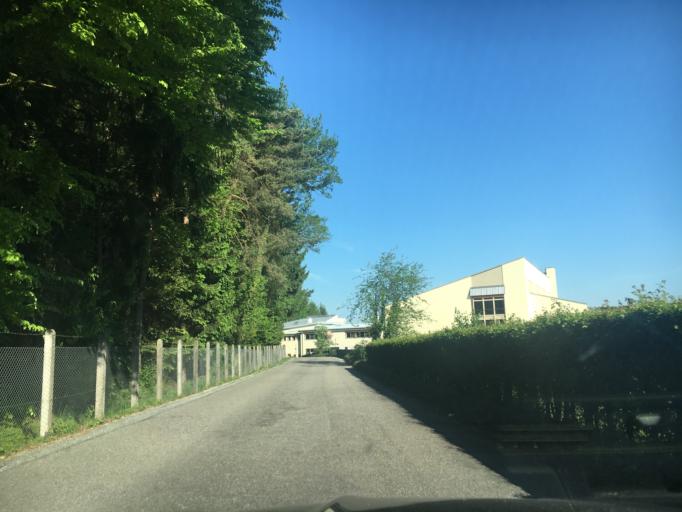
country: DE
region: Bavaria
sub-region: Upper Bavaria
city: Traunreut
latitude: 47.9579
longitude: 12.6148
